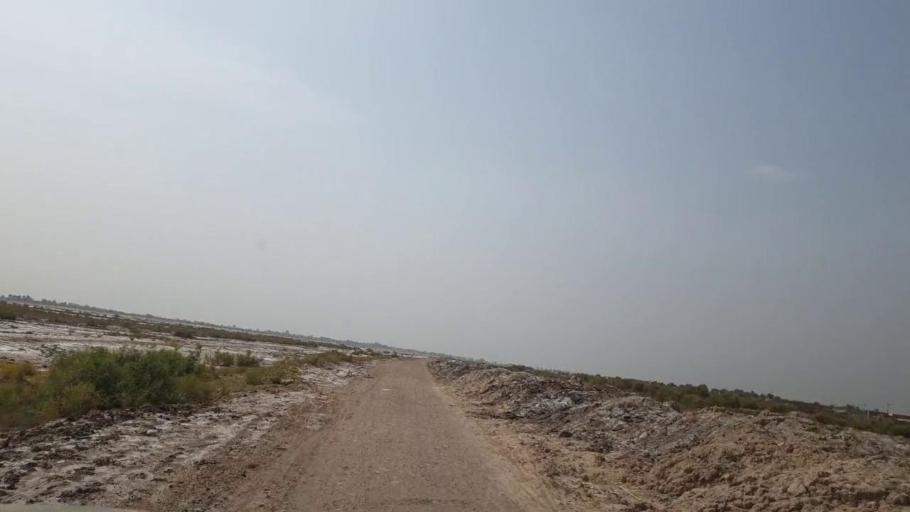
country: PK
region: Sindh
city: Dokri
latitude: 27.4220
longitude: 68.2051
